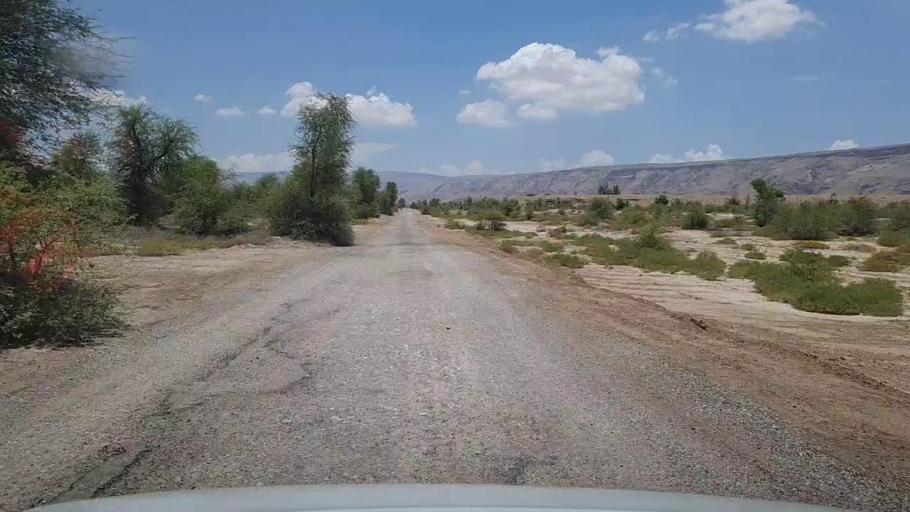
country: PK
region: Sindh
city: Bhan
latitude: 26.2747
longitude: 67.5253
